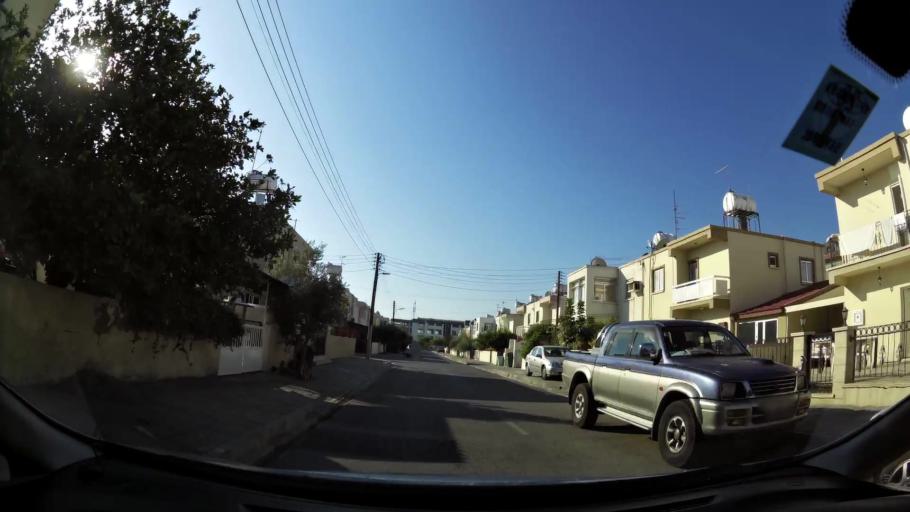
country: CY
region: Lefkosia
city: Nicosia
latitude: 35.2096
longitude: 33.3432
